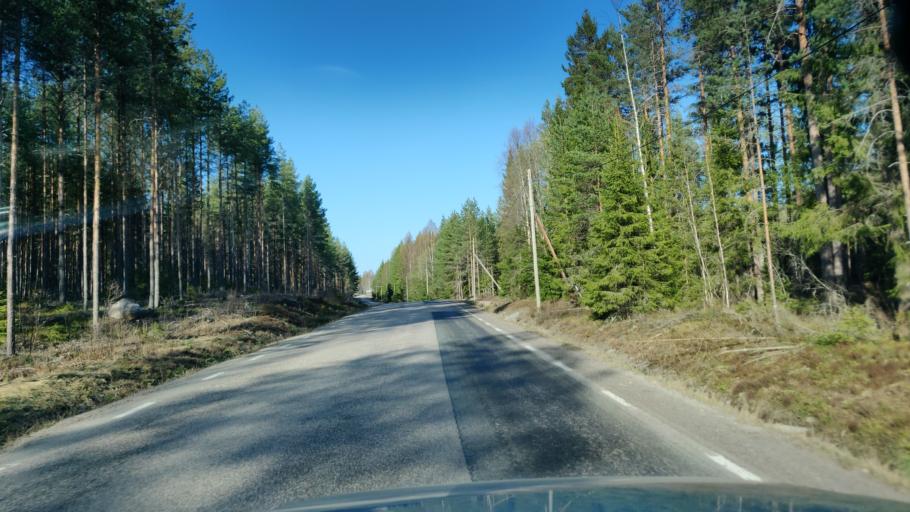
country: SE
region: Vaermland
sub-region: Sunne Kommun
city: Sunne
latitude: 59.9807
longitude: 13.2557
